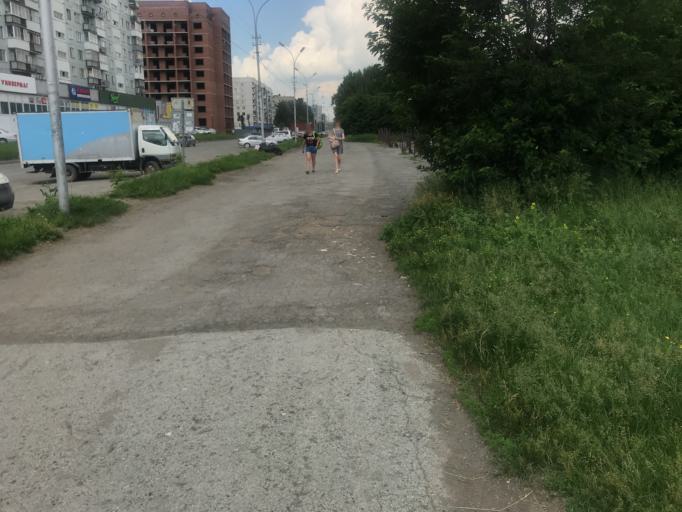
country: RU
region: Novosibirsk
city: Krasnoobsk
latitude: 54.9403
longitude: 82.9135
